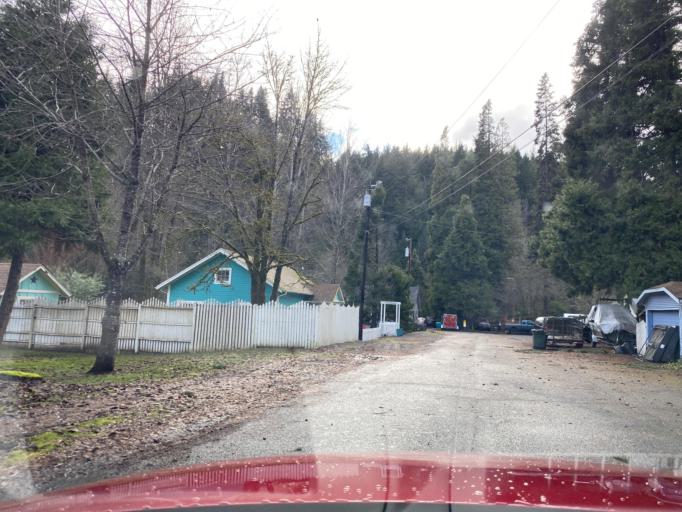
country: US
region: Oregon
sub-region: Lane County
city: Oakridge
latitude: 43.7579
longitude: -122.4950
